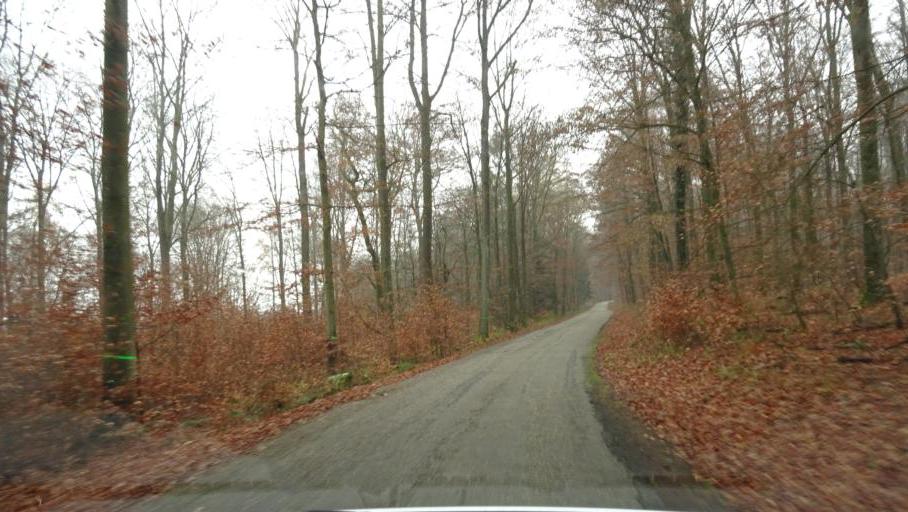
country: DE
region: Baden-Wuerttemberg
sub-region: Karlsruhe Region
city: Huffenhardt
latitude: 49.3205
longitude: 9.0805
